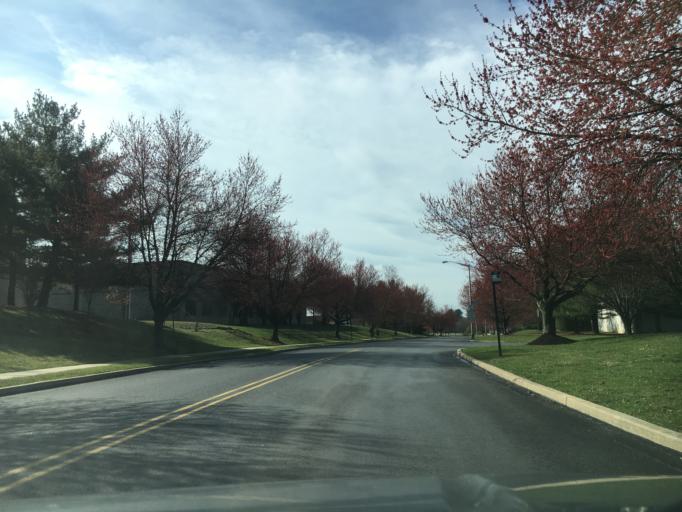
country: US
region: Pennsylvania
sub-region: Northampton County
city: Bath
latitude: 40.6774
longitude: -75.3828
